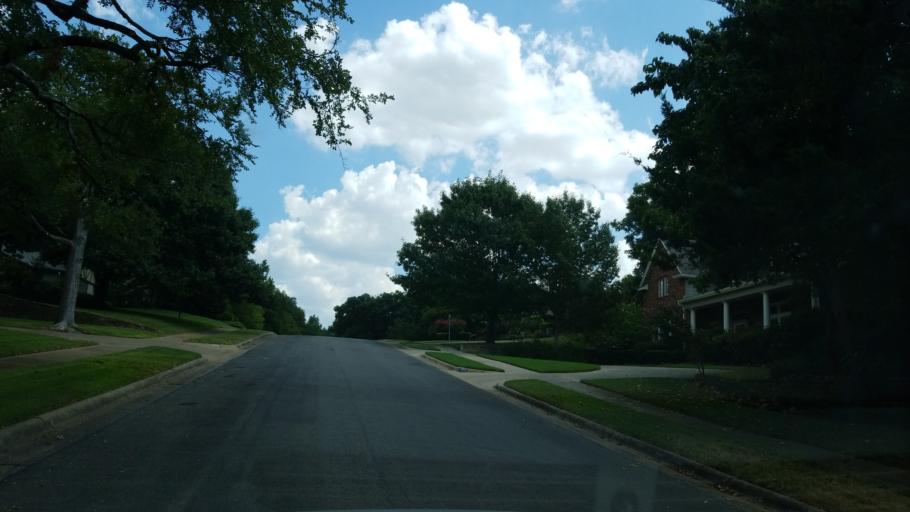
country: US
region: Texas
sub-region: Dallas County
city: Cockrell Hill
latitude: 32.7544
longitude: -96.8511
